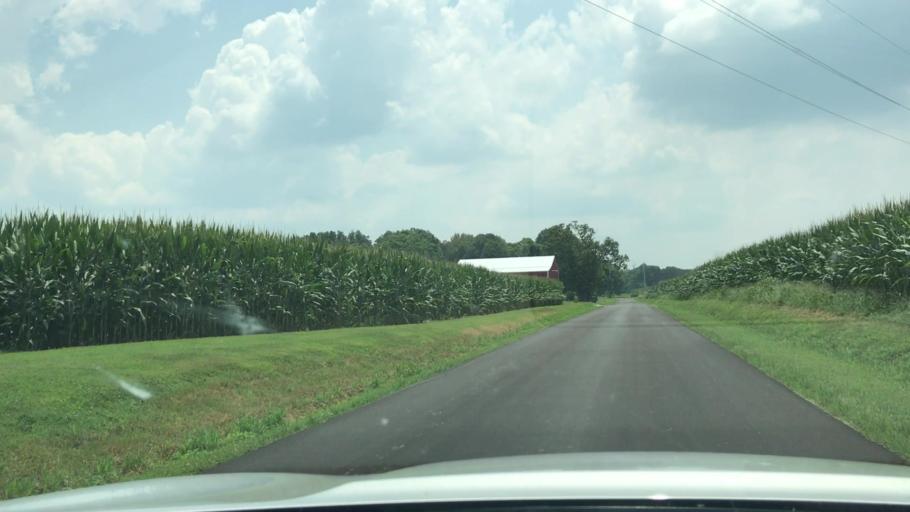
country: US
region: Kentucky
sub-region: Todd County
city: Elkton
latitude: 36.7771
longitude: -87.1450
